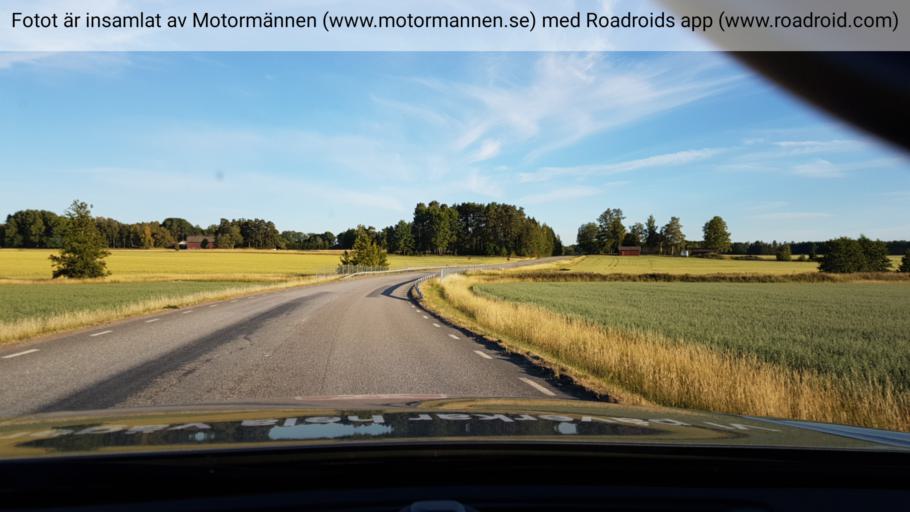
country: SE
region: Vaestmanland
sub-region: Vasteras
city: Skultuna
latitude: 59.7785
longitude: 16.4625
